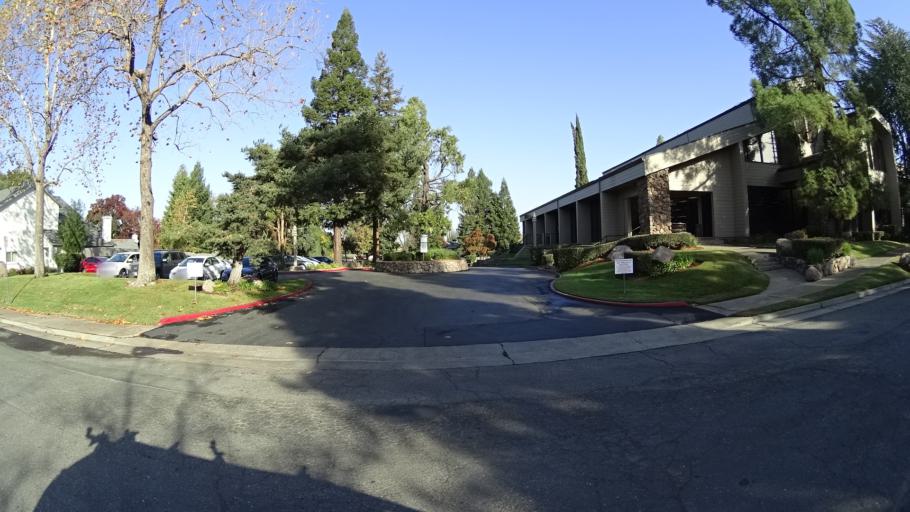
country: US
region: California
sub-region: Sacramento County
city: Citrus Heights
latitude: 38.6921
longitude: -121.2730
